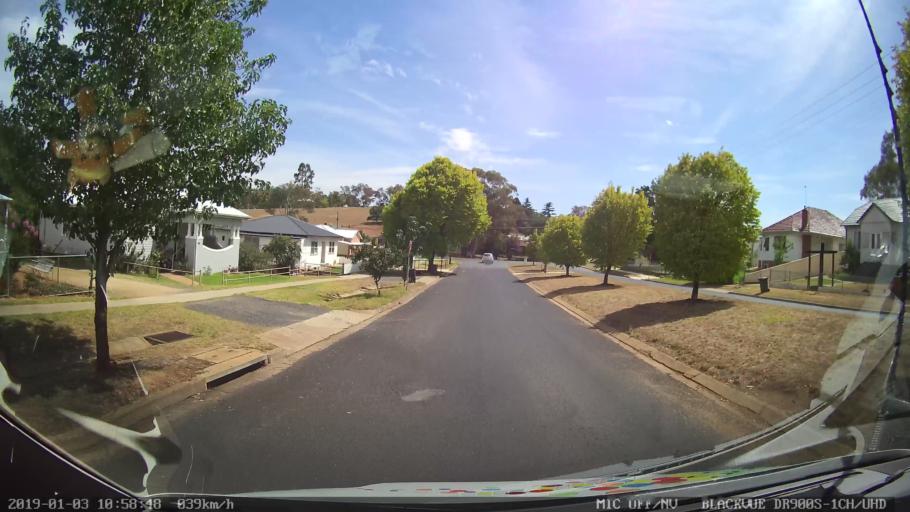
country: AU
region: New South Wales
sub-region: Young
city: Young
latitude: -34.3090
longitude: 148.2968
